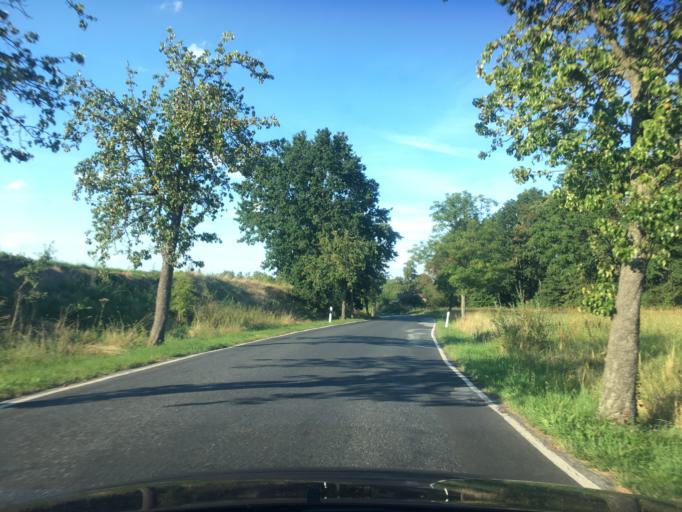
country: DE
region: Saxony
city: Goerlitz
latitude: 51.2102
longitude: 14.9989
